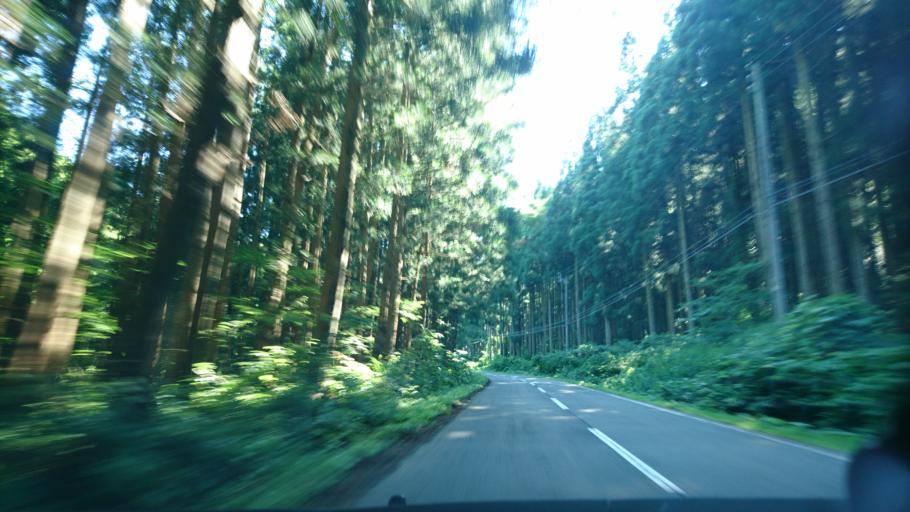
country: JP
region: Akita
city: Kakunodatemachi
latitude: 39.7081
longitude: 140.6059
